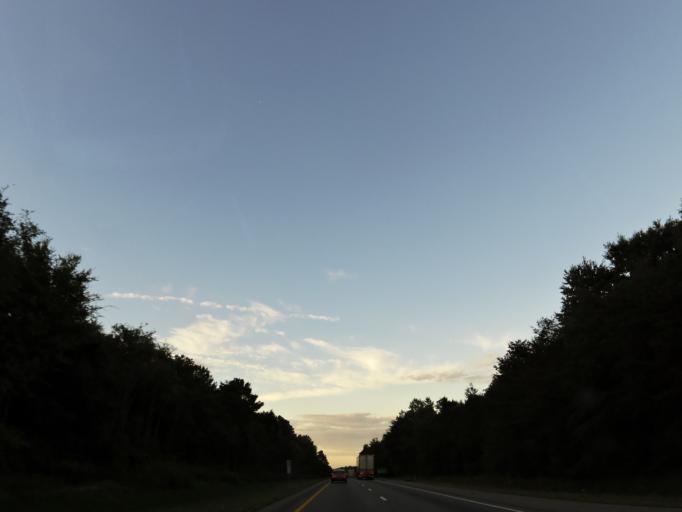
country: US
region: Tennessee
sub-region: McMinn County
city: Athens
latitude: 35.4027
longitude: -84.7083
